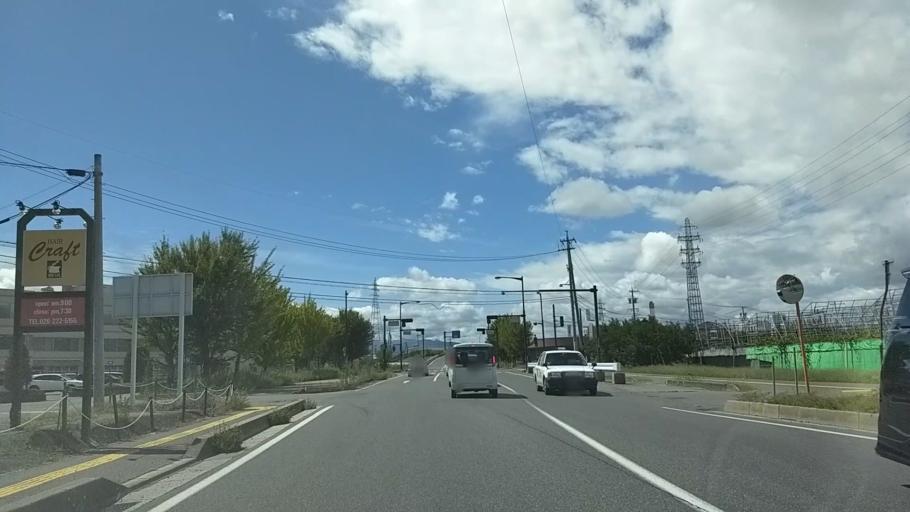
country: JP
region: Nagano
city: Nagano-shi
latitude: 36.6265
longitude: 138.2341
